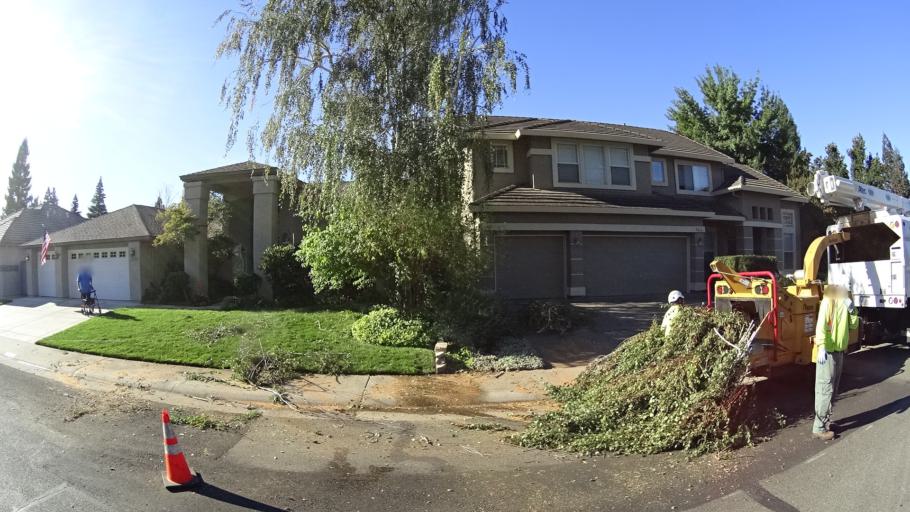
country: US
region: California
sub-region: Sacramento County
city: Elk Grove
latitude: 38.4276
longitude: -121.3789
